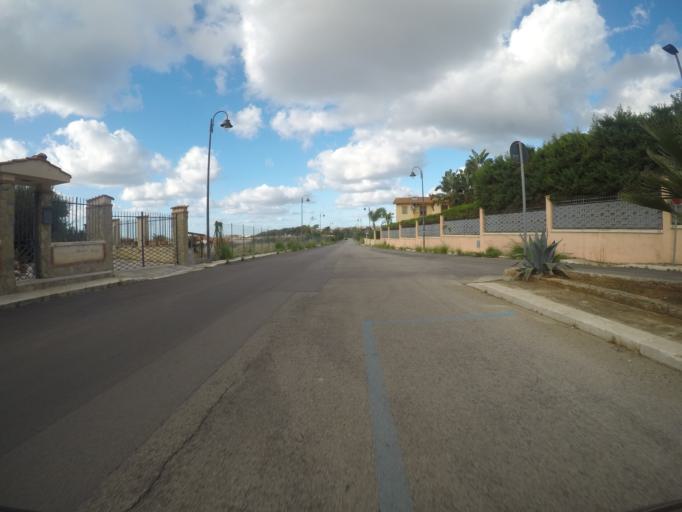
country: IT
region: Sicily
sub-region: Palermo
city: Isola delle Femmine
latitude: 38.1898
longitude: 13.2450
